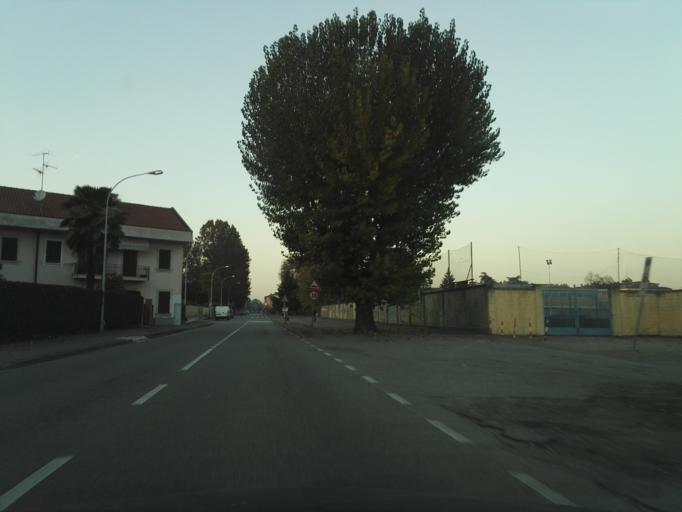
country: IT
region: Lombardy
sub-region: Citta metropolitana di Milano
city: Mezzate
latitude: 45.4418
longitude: 9.2947
